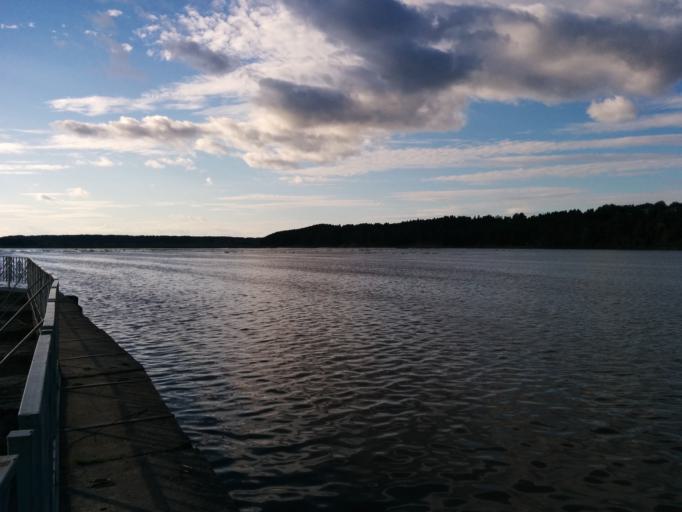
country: RU
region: Perm
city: Kudymkar
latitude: 59.0109
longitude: 54.6470
